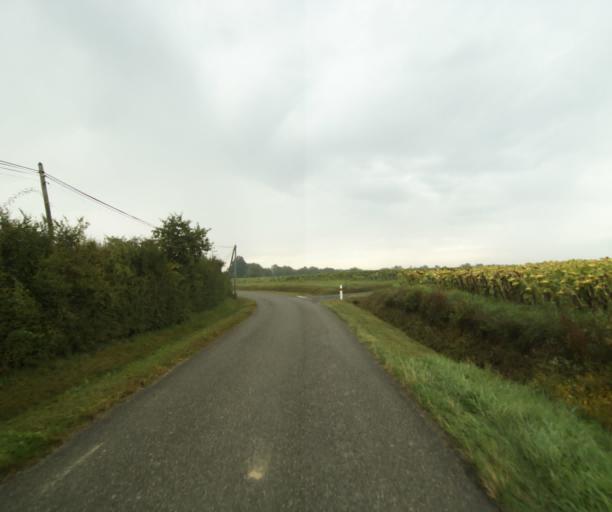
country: FR
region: Midi-Pyrenees
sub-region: Departement du Gers
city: Cazaubon
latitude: 43.9207
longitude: -0.1098
